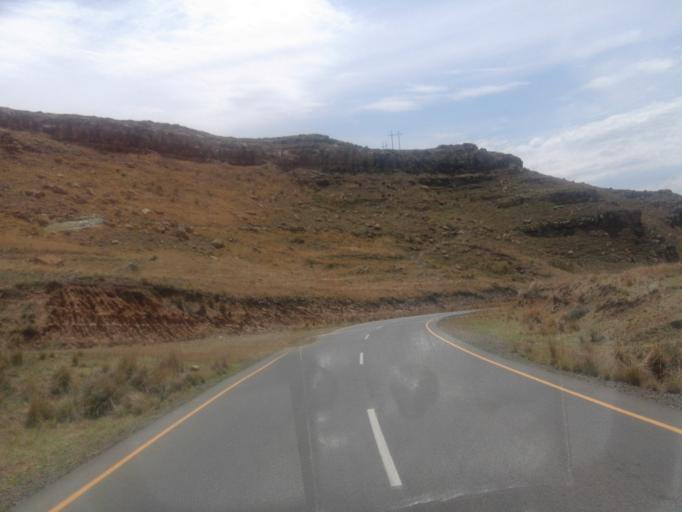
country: LS
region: Qacha's Nek
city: Qacha's Nek
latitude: -30.1048
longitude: 28.6570
